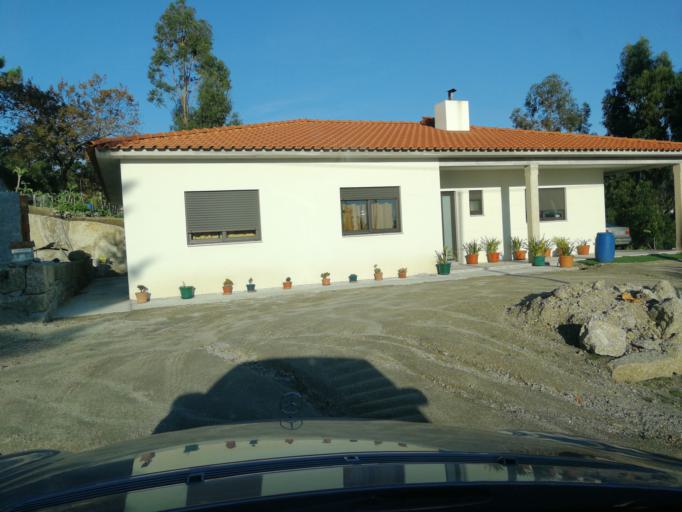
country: PT
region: Braga
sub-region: Braga
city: Oliveira
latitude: 41.4649
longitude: -8.4488
